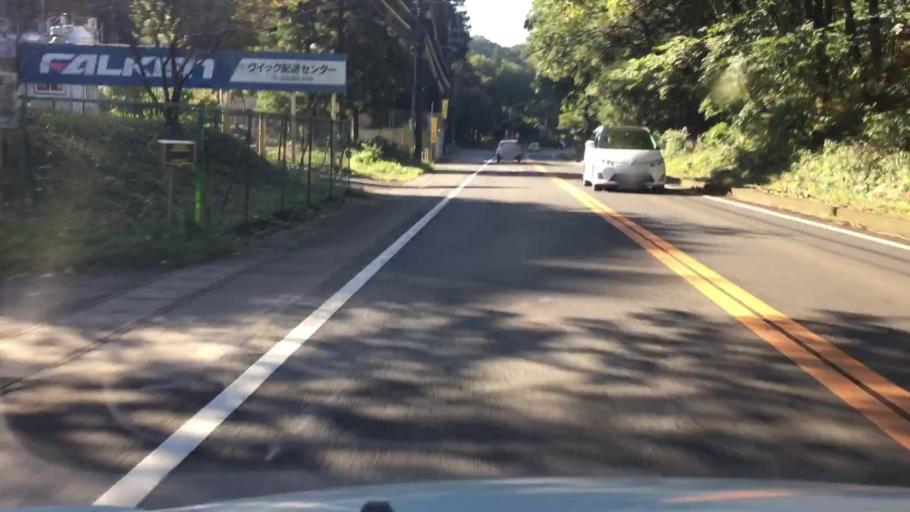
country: JP
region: Tochigi
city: Ujiie
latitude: 36.7029
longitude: 140.0162
